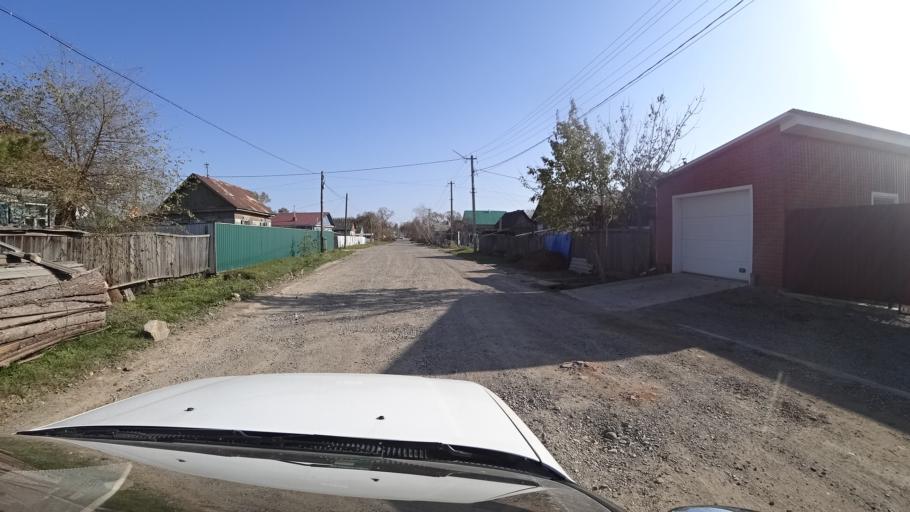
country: RU
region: Primorskiy
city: Dal'nerechensk
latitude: 45.9249
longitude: 133.7235
